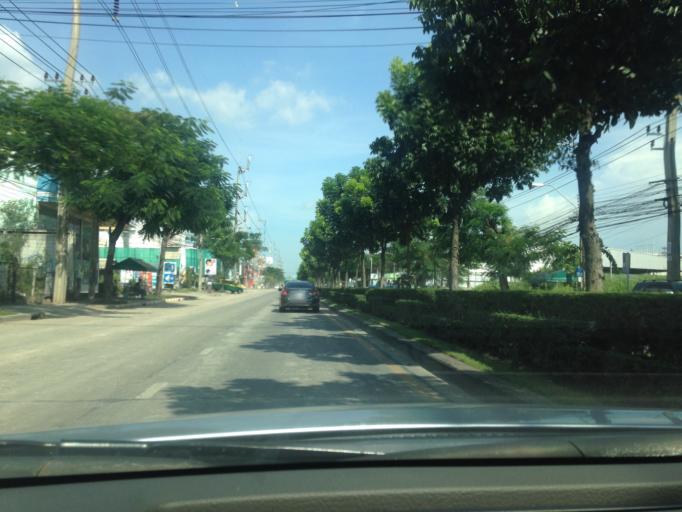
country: TH
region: Bangkok
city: Lat Krabang
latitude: 13.7223
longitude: 100.7307
